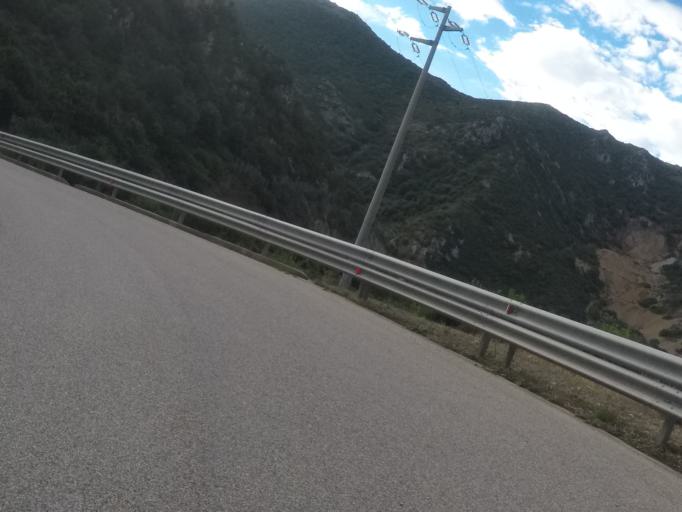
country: IT
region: Sardinia
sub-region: Provincia di Carbonia-Iglesias
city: Buggerru
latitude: 39.3349
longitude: 8.4400
